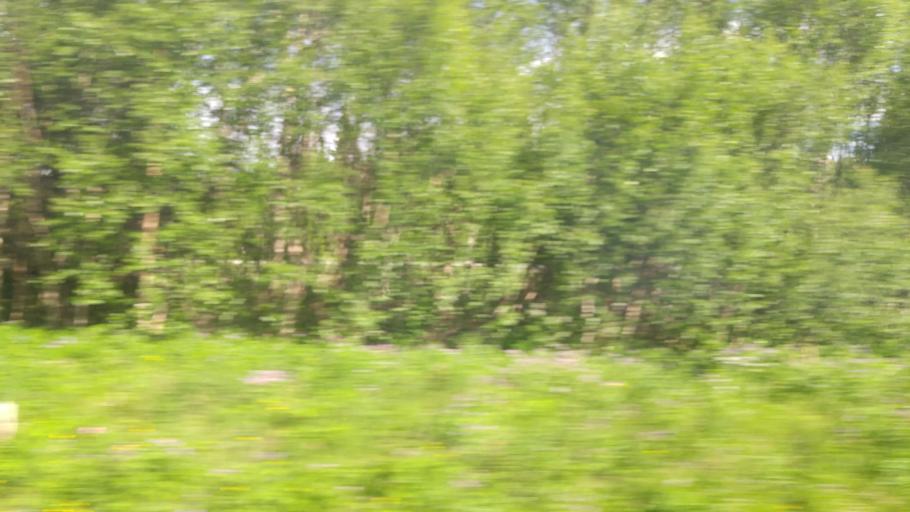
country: SE
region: Jaemtland
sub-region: Are Kommun
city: Are
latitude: 63.3100
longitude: 12.4762
